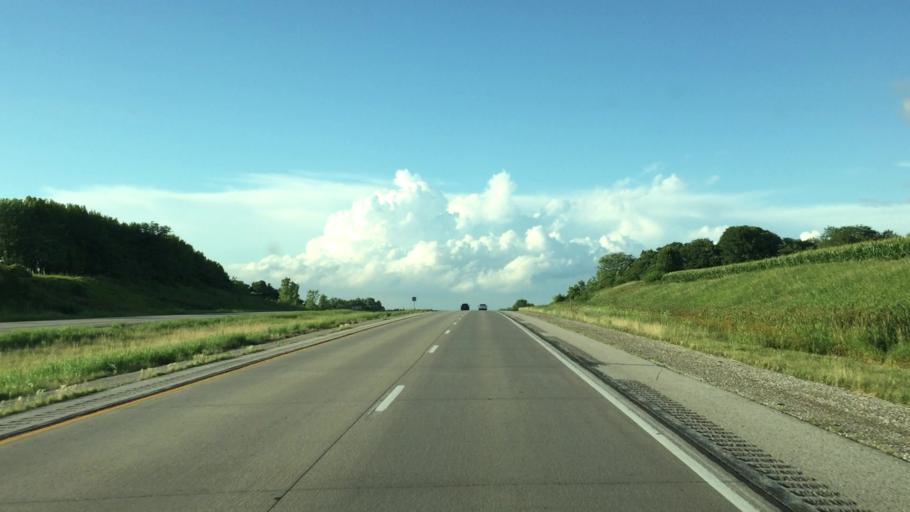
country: US
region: Iowa
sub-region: Johnson County
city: University Heights
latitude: 41.5388
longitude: -91.5483
